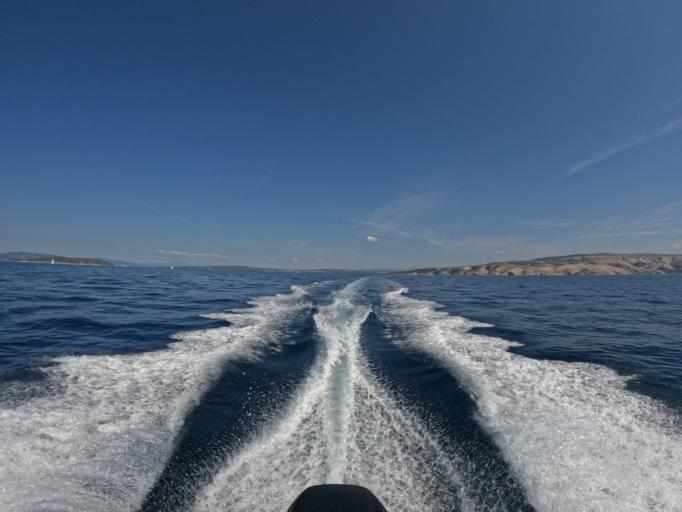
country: HR
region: Primorsko-Goranska
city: Punat
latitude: 44.9326
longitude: 14.6165
